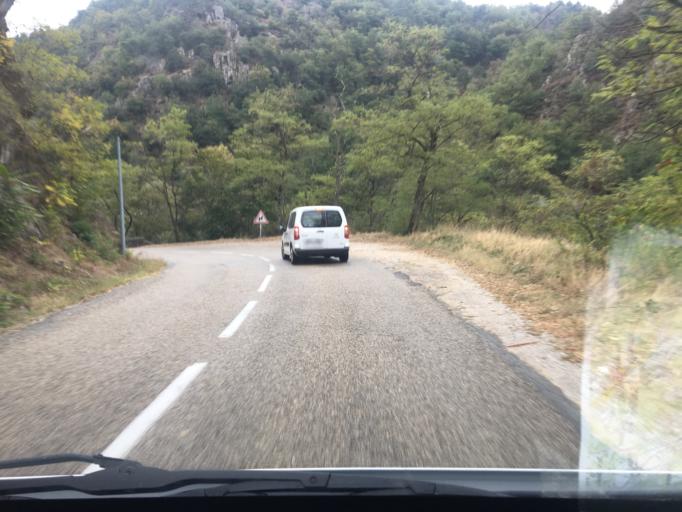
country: FR
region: Rhone-Alpes
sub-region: Departement de l'Ardeche
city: Saint-Jean-de-Muzols
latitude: 45.0590
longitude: 4.7312
